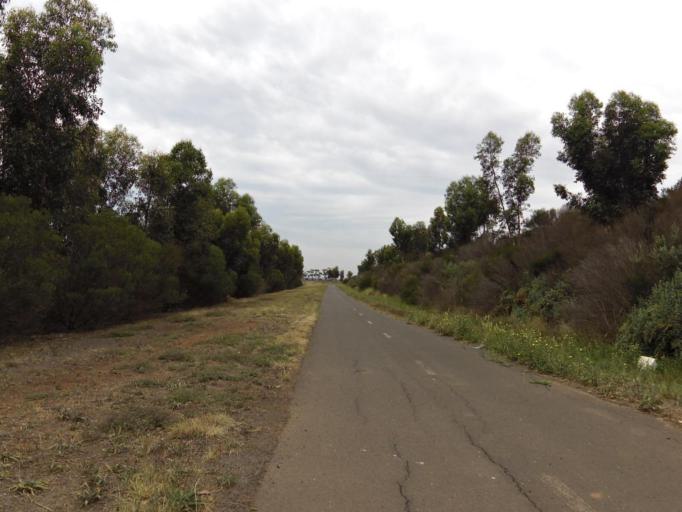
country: AU
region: Victoria
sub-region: Brimbank
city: Derrimut
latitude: -37.7784
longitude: 144.7475
